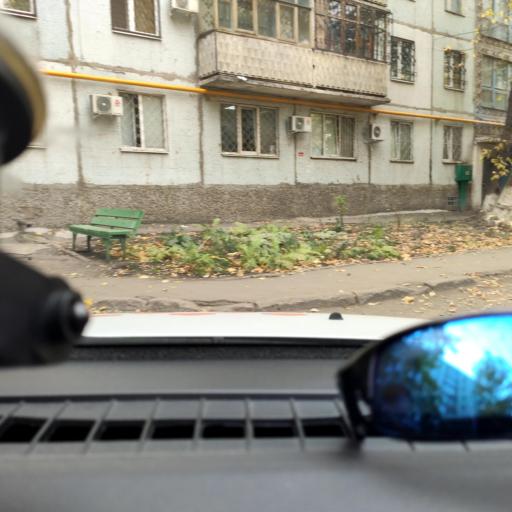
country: RU
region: Samara
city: Samara
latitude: 53.2585
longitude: 50.2275
